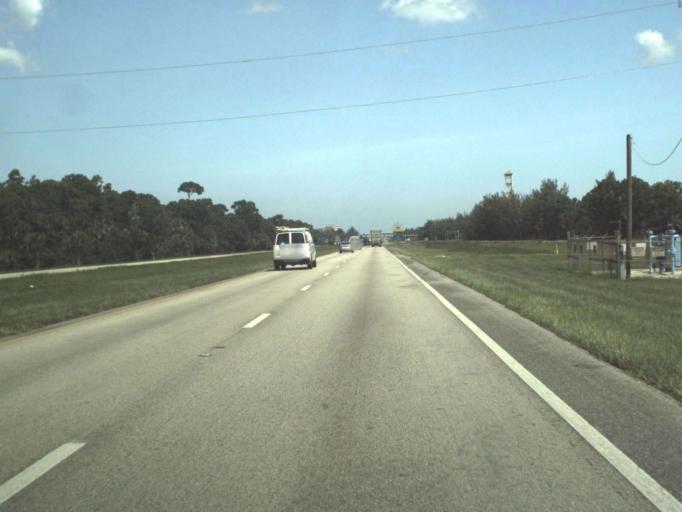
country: US
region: Florida
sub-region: Palm Beach County
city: Palm Beach Gardens
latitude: 26.8033
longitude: -80.1426
